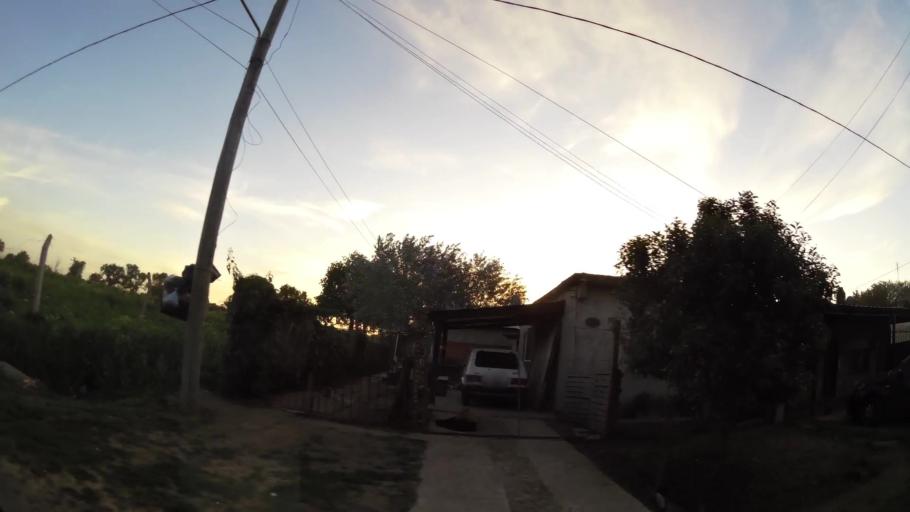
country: AR
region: Buenos Aires
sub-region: Partido de Quilmes
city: Quilmes
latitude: -34.7901
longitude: -58.2247
